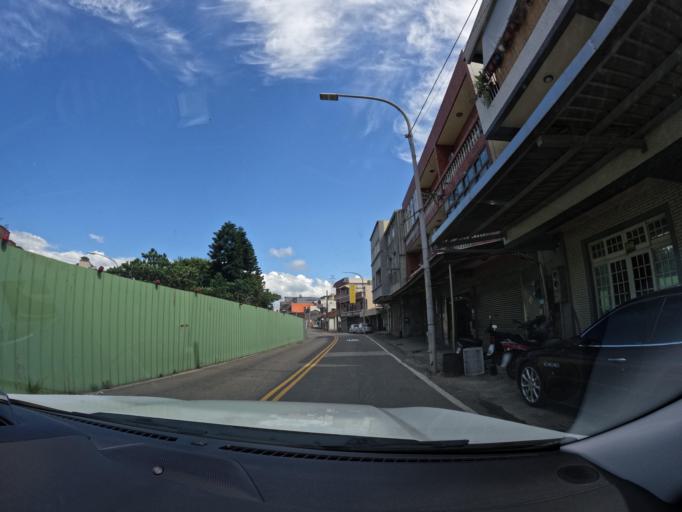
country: TW
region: Taiwan
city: Taoyuan City
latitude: 25.1181
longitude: 121.2981
